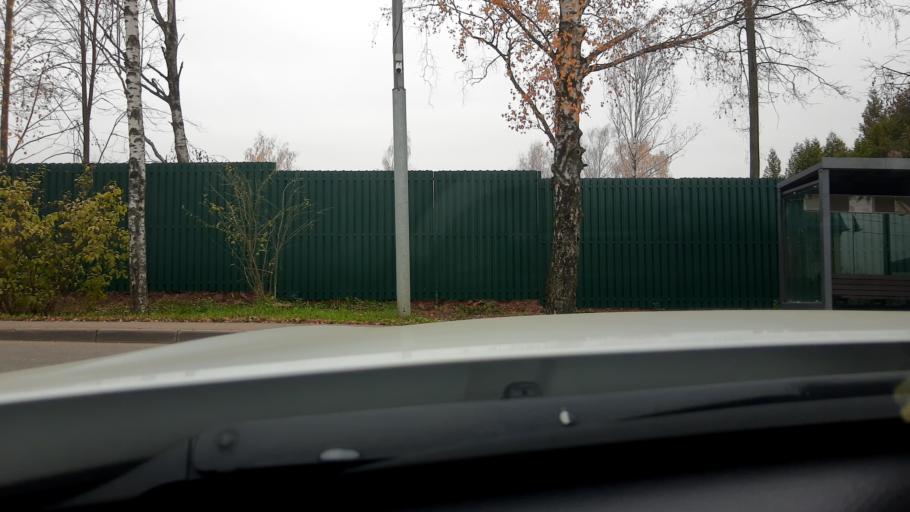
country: RU
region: Moskovskaya
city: Dolgoprudnyy
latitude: 55.9519
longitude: 37.4732
